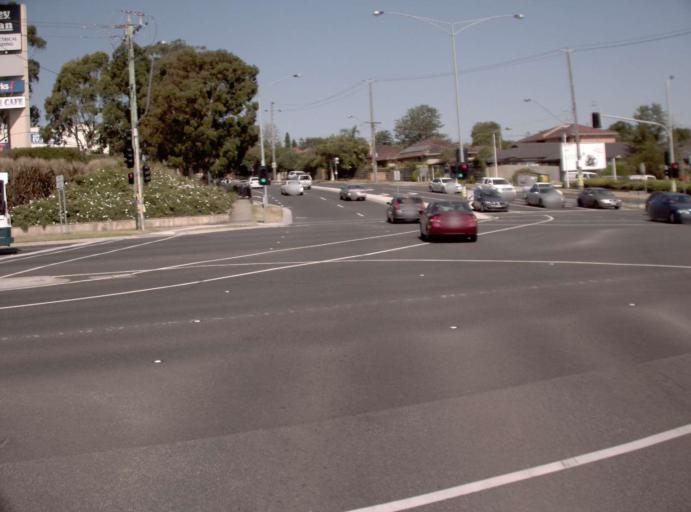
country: AU
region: Victoria
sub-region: Monash
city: Chadstone
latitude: -37.8800
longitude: 145.0905
